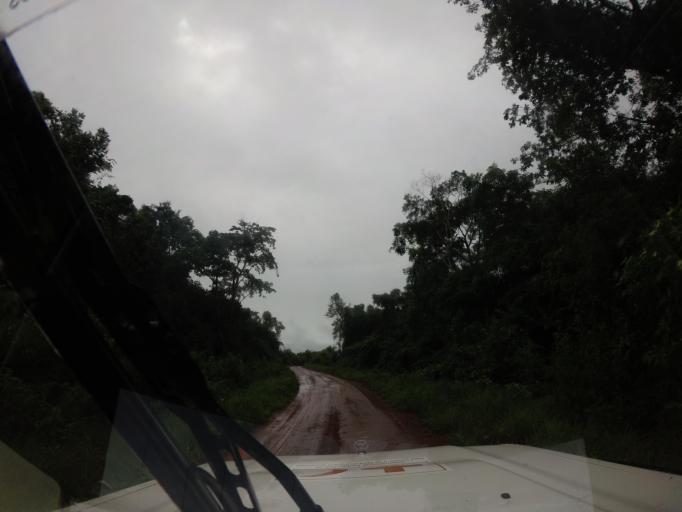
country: SL
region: Eastern Province
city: Kenema
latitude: 7.7333
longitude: -11.1897
